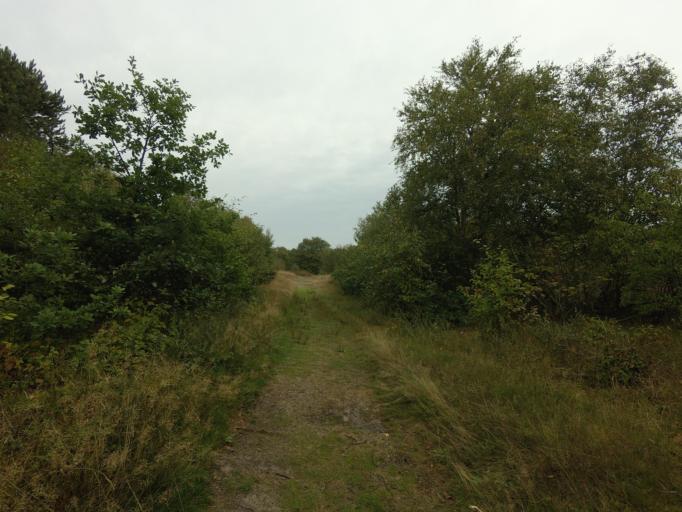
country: NL
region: Friesland
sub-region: Gemeente Schiermonnikoog
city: Schiermonnikoog
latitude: 53.4862
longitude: 6.1677
